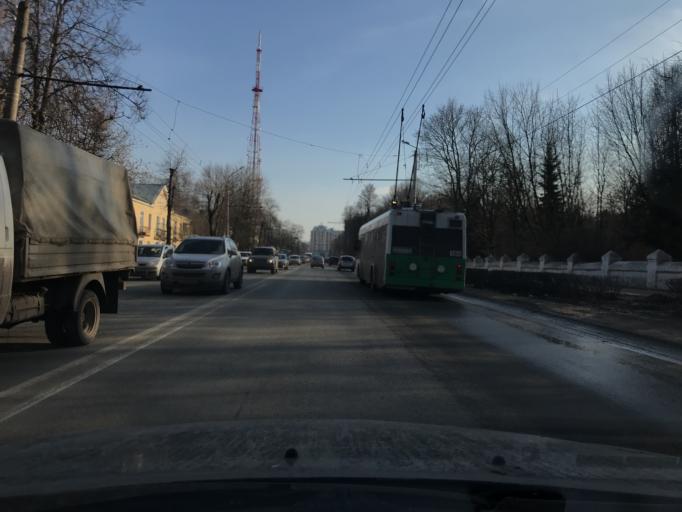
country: RU
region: Kaluga
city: Kaluga
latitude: 54.5258
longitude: 36.2611
